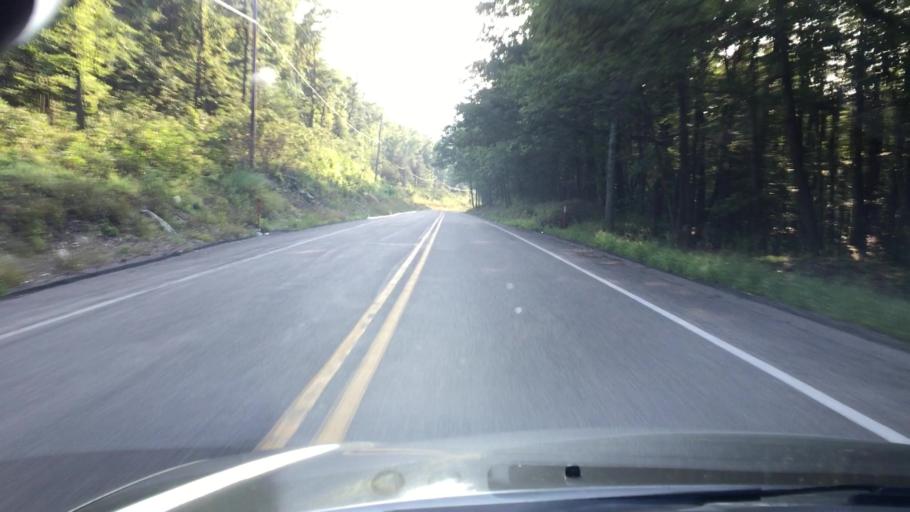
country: US
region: Pennsylvania
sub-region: Carbon County
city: Weatherly
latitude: 40.9121
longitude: -75.8398
